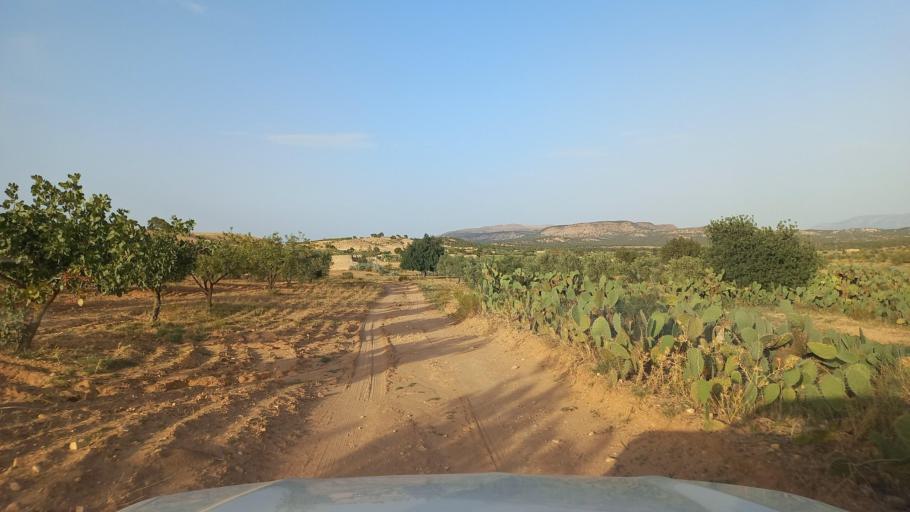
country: TN
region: Al Qasrayn
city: Sbiba
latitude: 35.4078
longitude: 8.8976
